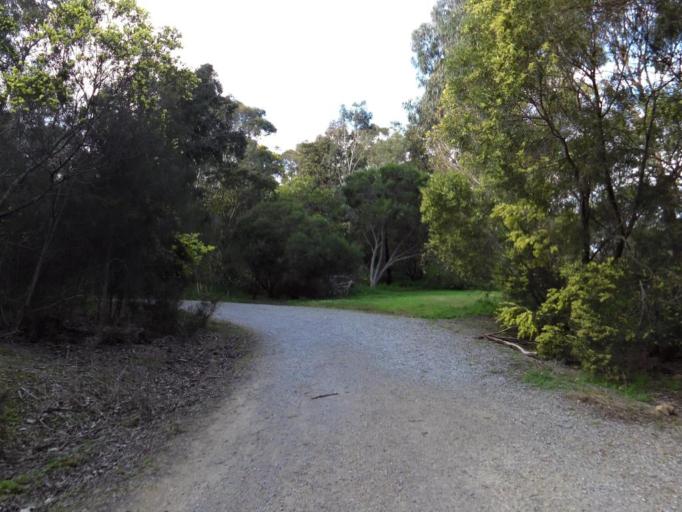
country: AU
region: Victoria
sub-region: Whitehorse
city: Vermont South
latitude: -37.8640
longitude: 145.1952
